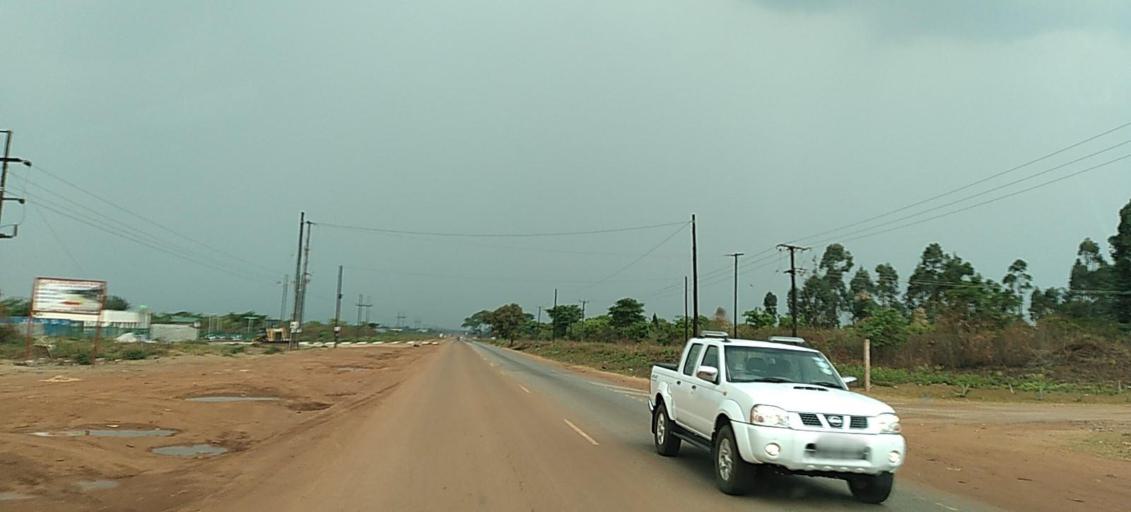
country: ZM
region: Copperbelt
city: Kalulushi
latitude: -12.8338
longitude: 28.1114
